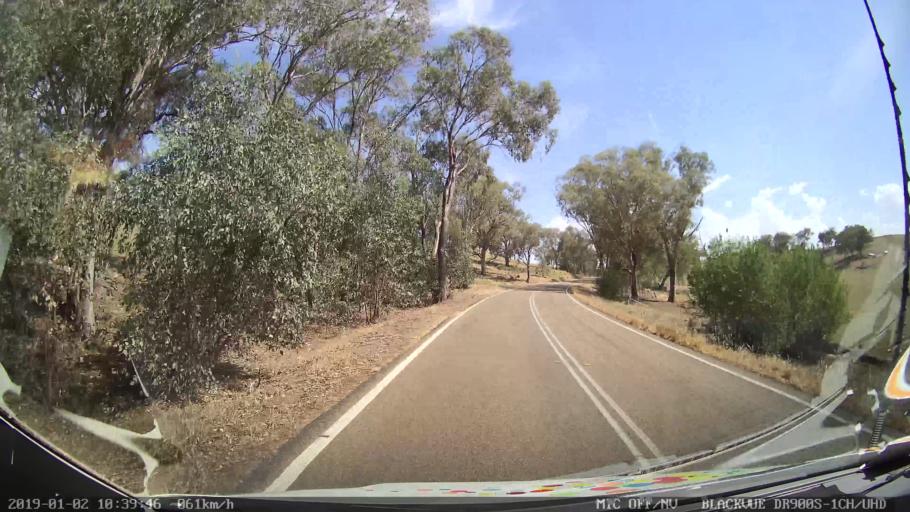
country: AU
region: New South Wales
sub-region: Gundagai
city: Gundagai
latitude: -34.8080
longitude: 148.3179
